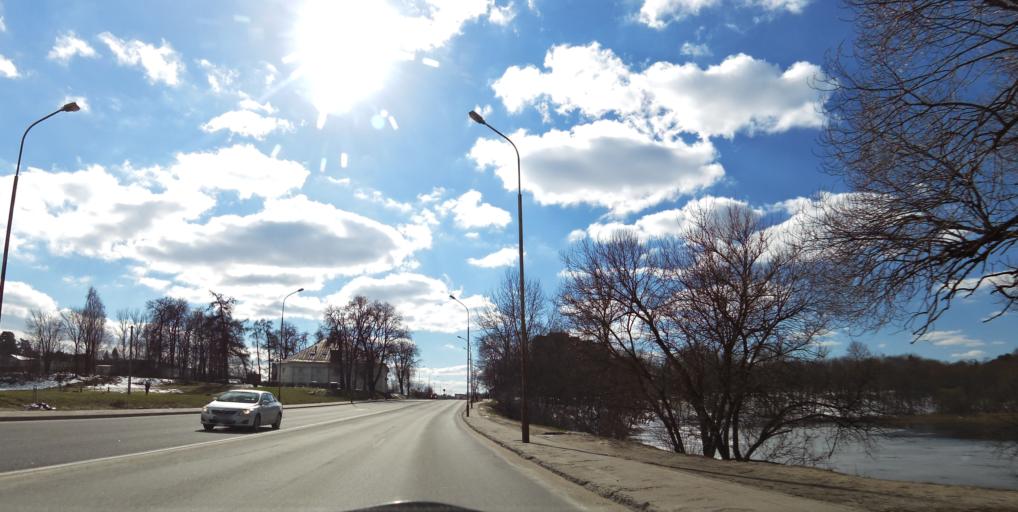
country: LT
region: Vilnius County
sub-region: Vilnius
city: Fabijoniskes
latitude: 54.7479
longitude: 25.2792
